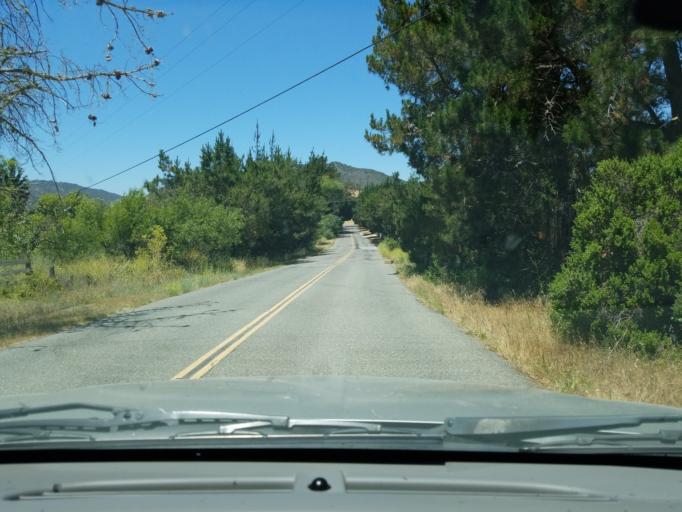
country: US
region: California
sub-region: Monterey County
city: Carmel Valley Village
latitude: 36.4415
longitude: -121.6443
